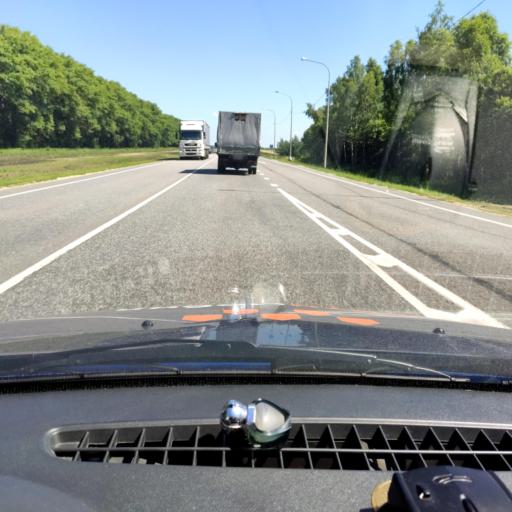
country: RU
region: Orjol
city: Pokrovskoye
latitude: 52.6410
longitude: 36.6721
